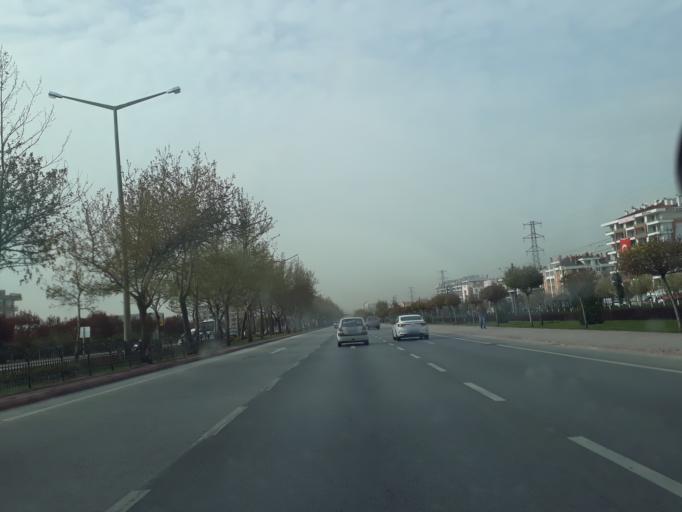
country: TR
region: Konya
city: Selcuklu
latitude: 37.9763
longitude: 32.5163
